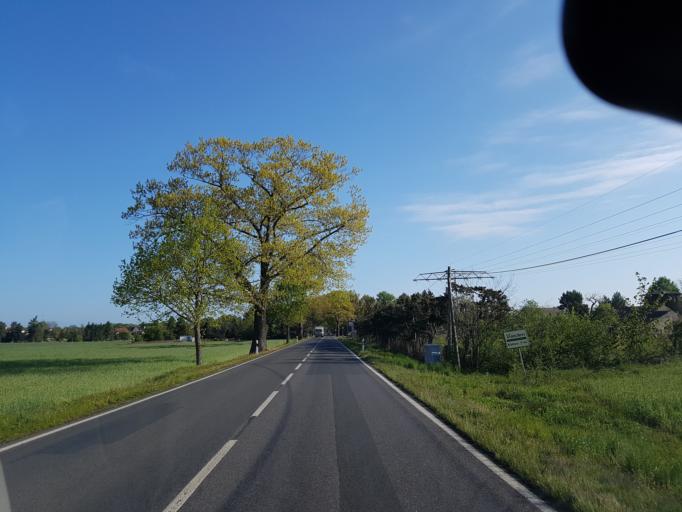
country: DE
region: Brandenburg
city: Altdobern
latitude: 51.6435
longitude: 14.0335
